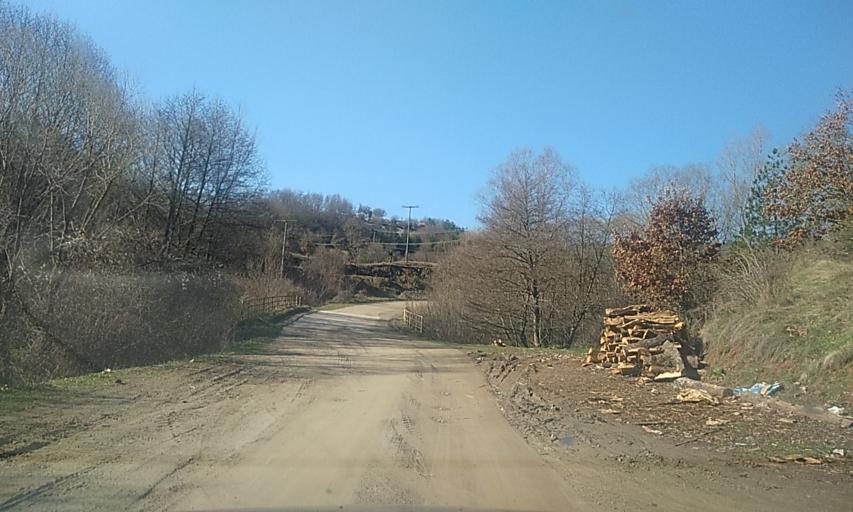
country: RS
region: Central Serbia
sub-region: Pcinjski Okrug
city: Bosilegrad
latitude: 42.3638
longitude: 22.4312
